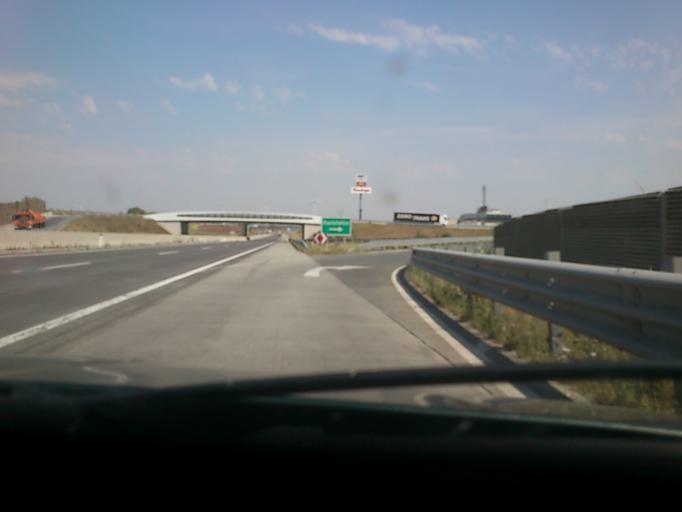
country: AT
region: Lower Austria
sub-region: Politischer Bezirk Ganserndorf
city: Aderklaa
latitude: 48.3083
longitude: 16.5119
